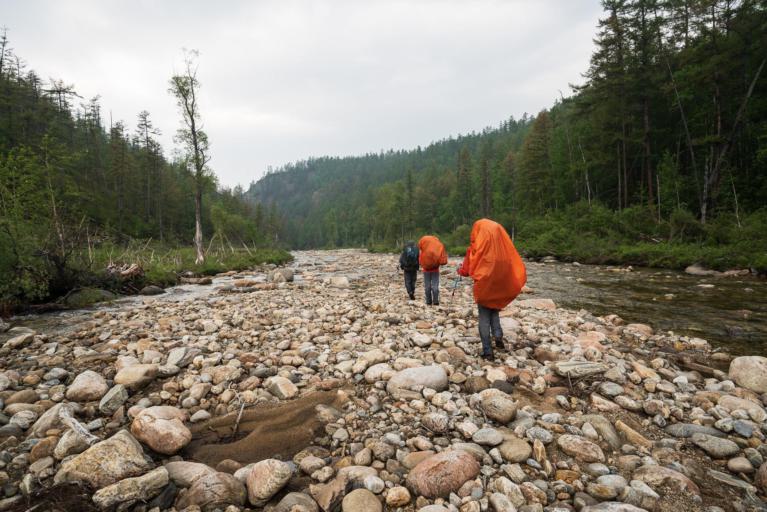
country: RU
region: Transbaikal Territory
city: Kuanda
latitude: 56.5130
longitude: 116.3945
